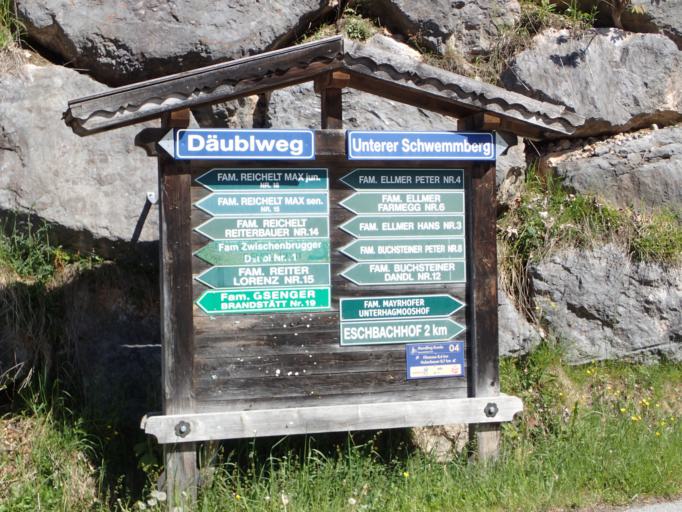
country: AT
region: Salzburg
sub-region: Politischer Bezirk Sankt Johann im Pongau
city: Forstau
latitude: 47.3970
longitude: 13.5135
